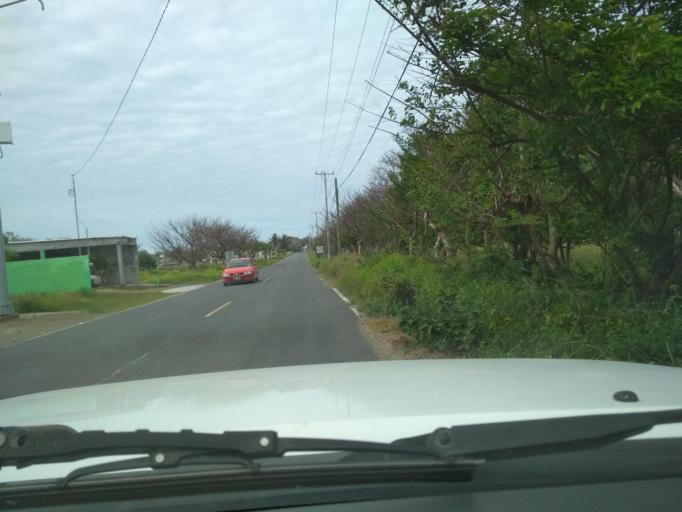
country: MX
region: Veracruz
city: Anton Lizardo
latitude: 19.0485
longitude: -95.9865
